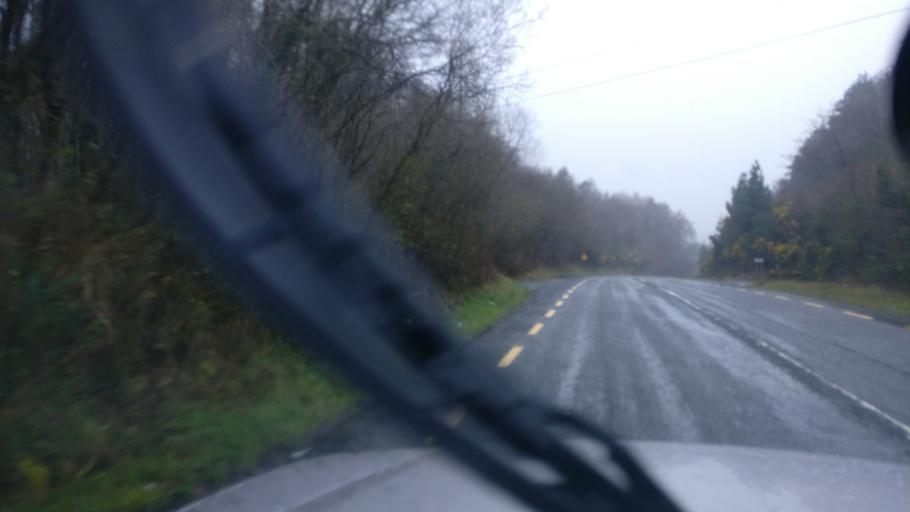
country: IE
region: Connaught
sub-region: County Galway
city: Loughrea
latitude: 53.1434
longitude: -8.4704
